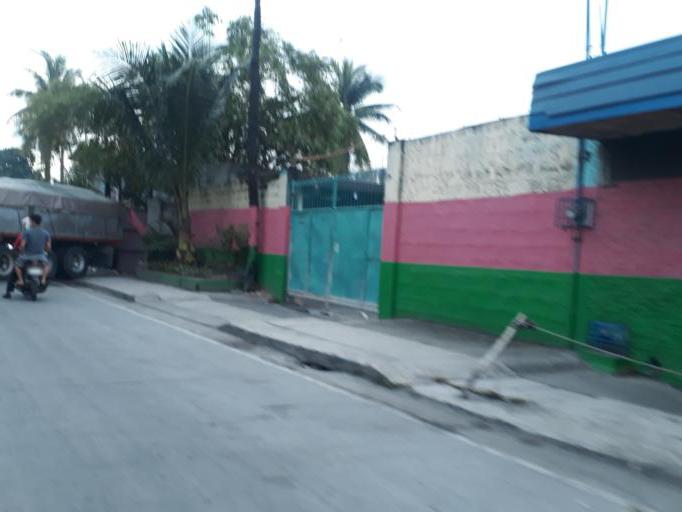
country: PH
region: Calabarzon
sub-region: Province of Rizal
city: Valenzuela
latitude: 14.6887
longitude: 120.9569
